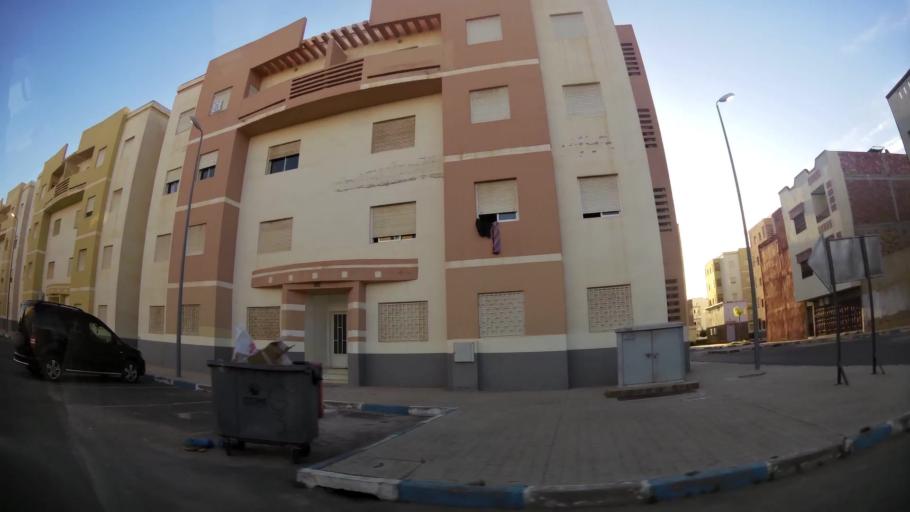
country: MA
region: Oriental
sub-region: Berkane-Taourirt
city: Madagh
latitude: 35.0792
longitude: -2.2368
